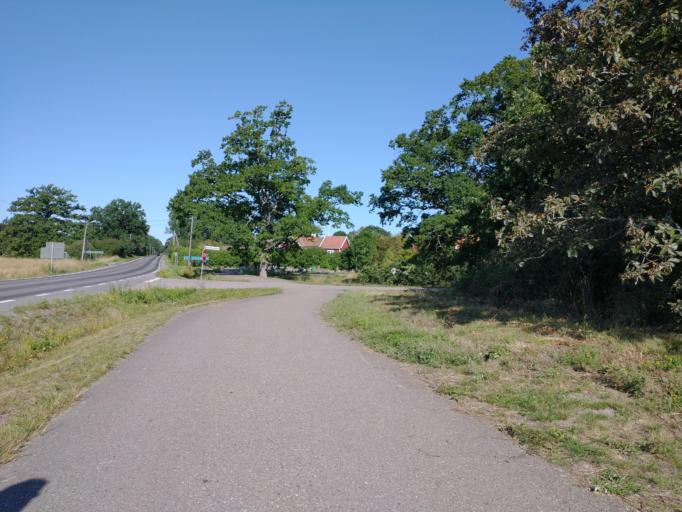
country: SE
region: Kalmar
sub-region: Kalmar Kommun
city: Lindsdal
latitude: 56.7810
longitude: 16.2826
